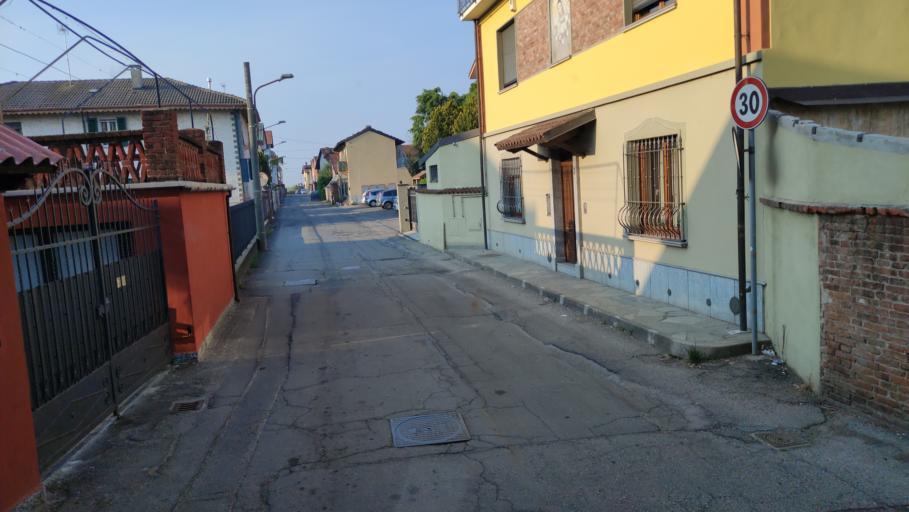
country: IT
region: Piedmont
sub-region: Provincia di Torino
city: Trofarello
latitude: 44.9855
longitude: 7.7313
